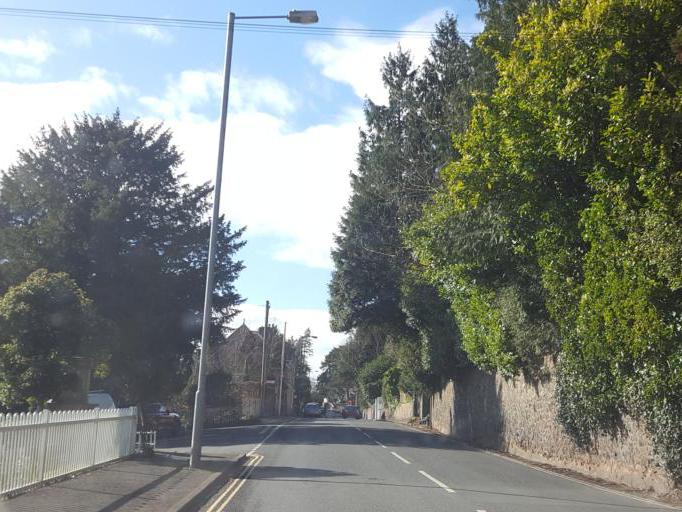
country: GB
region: England
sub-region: Worcestershire
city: Great Malvern
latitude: 52.0789
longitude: -2.3323
